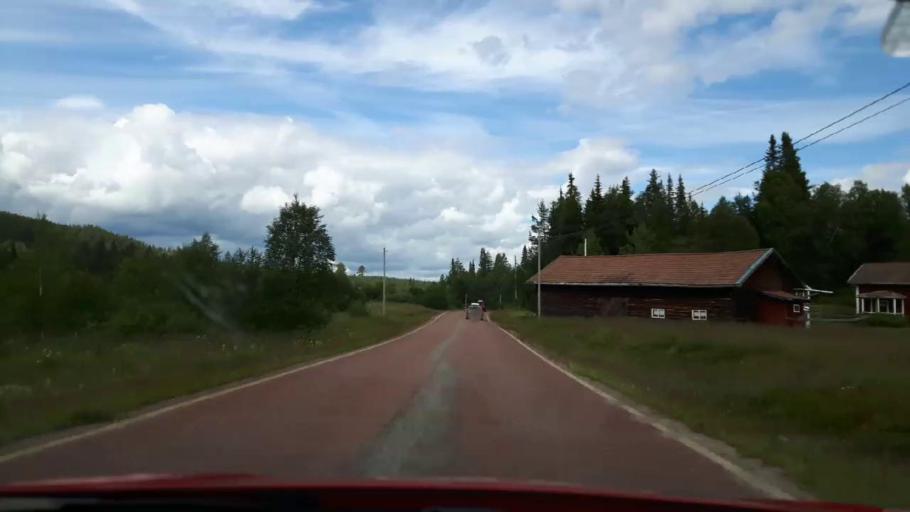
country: NO
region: Hedmark
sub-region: Trysil
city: Innbygda
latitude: 61.9972
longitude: 12.9812
